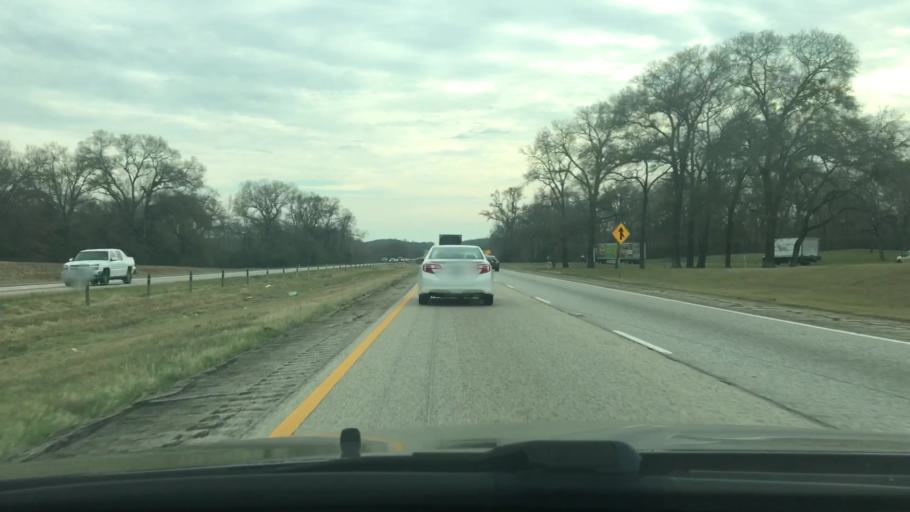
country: US
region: Texas
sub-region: Leon County
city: Centerville
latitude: 31.1954
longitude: -95.9936
